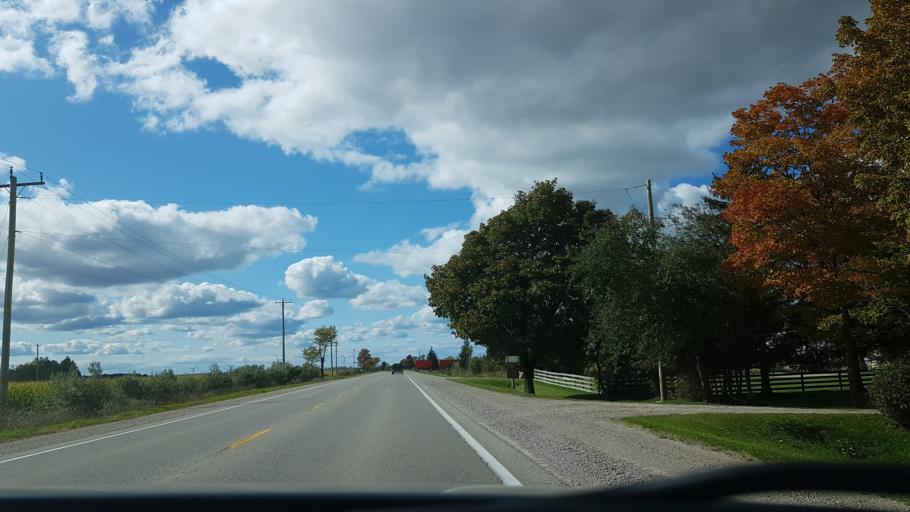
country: CA
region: Ontario
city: Bluewater
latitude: 43.3437
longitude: -81.6579
